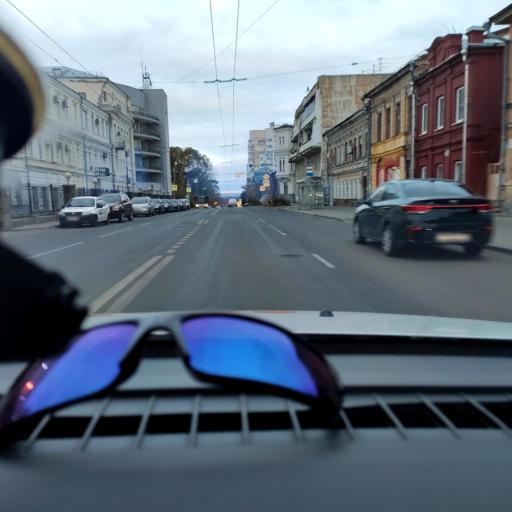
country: RU
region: Samara
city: Rozhdestveno
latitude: 53.1834
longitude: 50.0853
